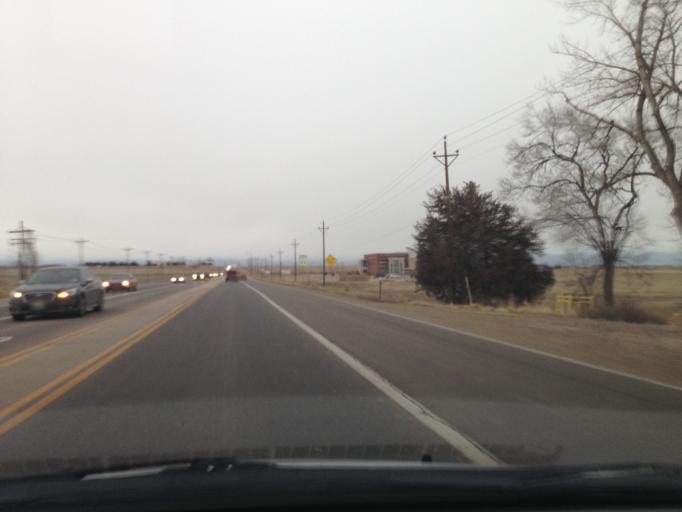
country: US
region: Colorado
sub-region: Weld County
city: Dacono
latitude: 40.0878
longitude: -104.9617
